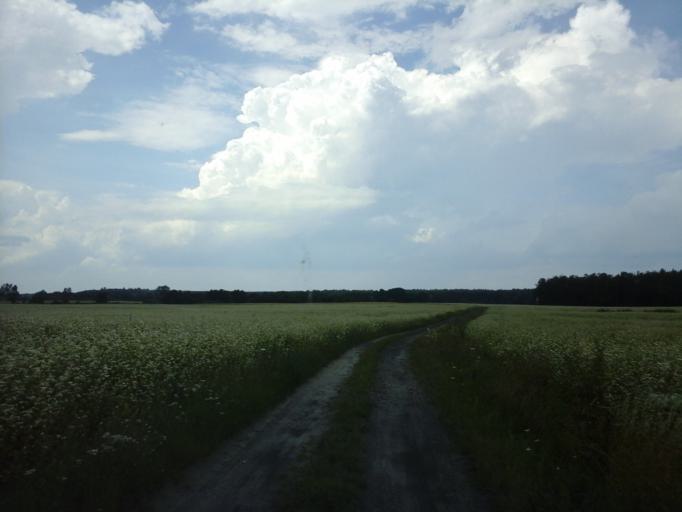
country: PL
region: West Pomeranian Voivodeship
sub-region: Powiat choszczenski
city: Bierzwnik
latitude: 53.0562
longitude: 15.7239
